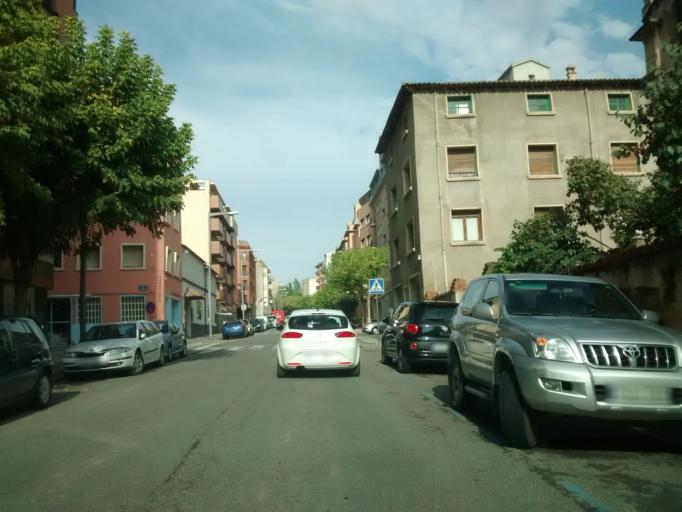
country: ES
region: Aragon
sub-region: Provincia de Huesca
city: Barbastro
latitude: 42.0372
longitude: 0.1286
